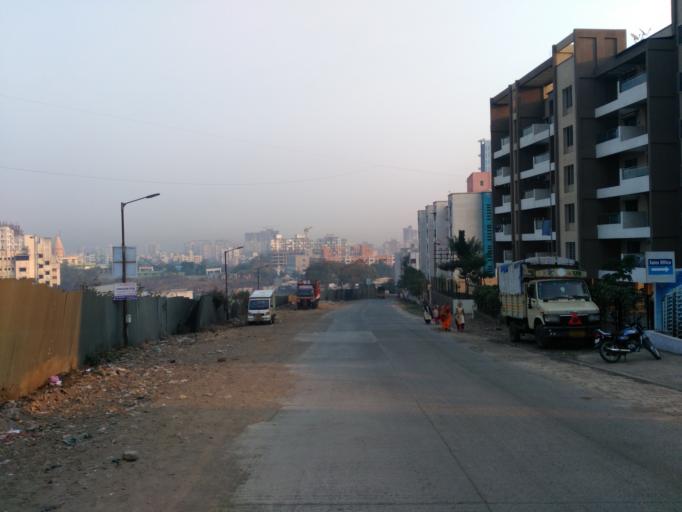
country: IN
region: Maharashtra
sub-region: Pune Division
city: Pune
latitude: 18.4479
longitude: 73.8792
